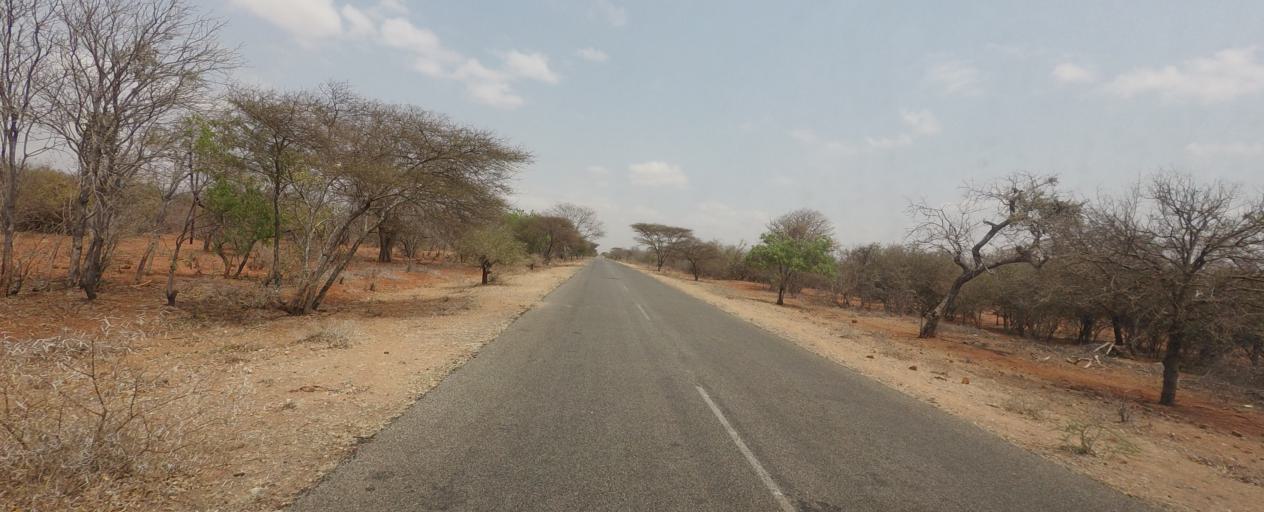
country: ZA
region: Limpopo
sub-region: Vhembe District Municipality
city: Mutale
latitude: -22.4212
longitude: 30.9214
